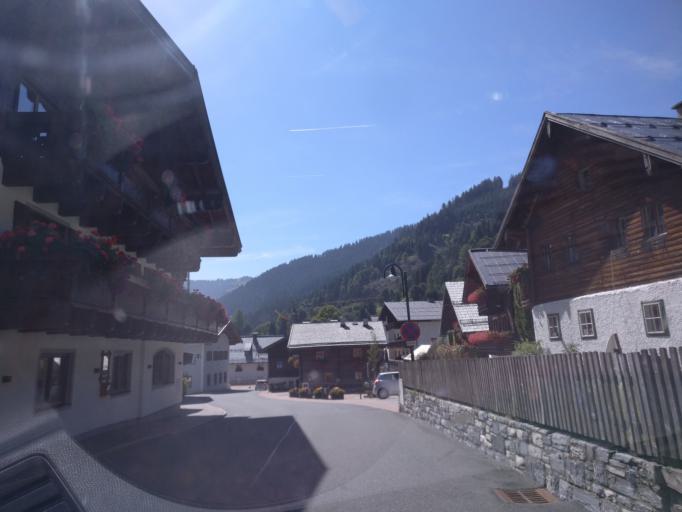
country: AT
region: Salzburg
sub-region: Politischer Bezirk Zell am See
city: Dienten am Hochkonig
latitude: 47.3830
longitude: 13.0034
